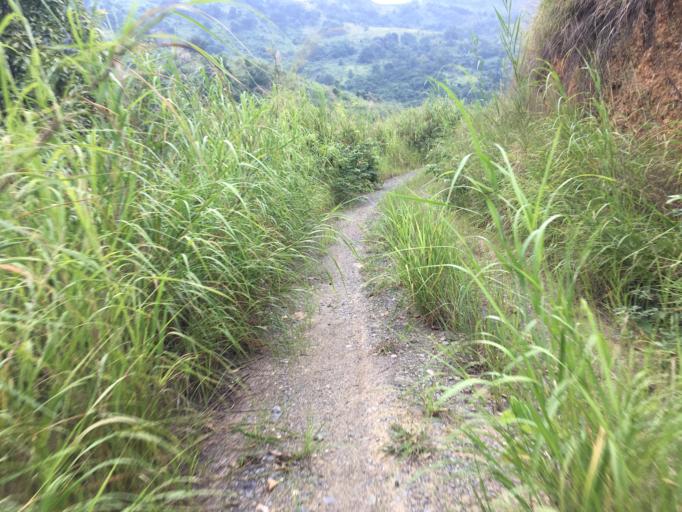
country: CN
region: Guangxi Zhuangzu Zizhiqu
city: Xinzhou
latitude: 25.1894
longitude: 105.8906
